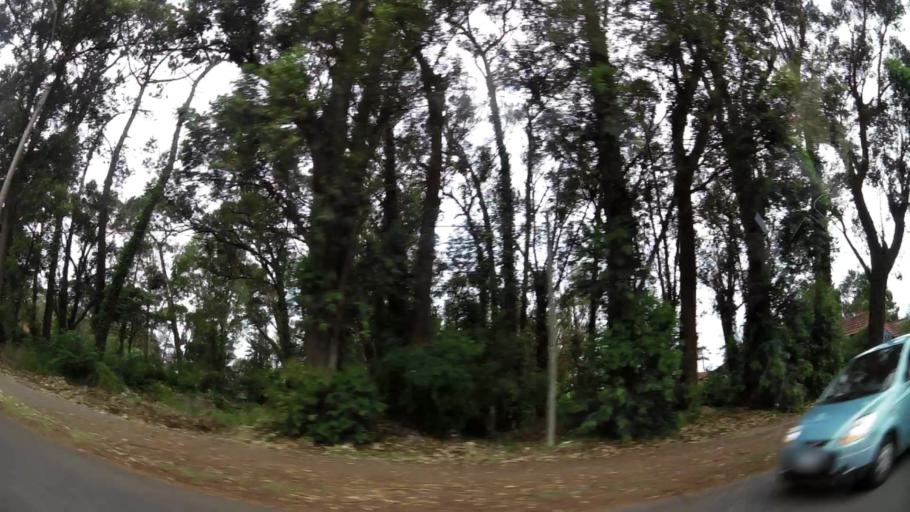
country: UY
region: Maldonado
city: Maldonado
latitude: -34.9111
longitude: -54.9793
